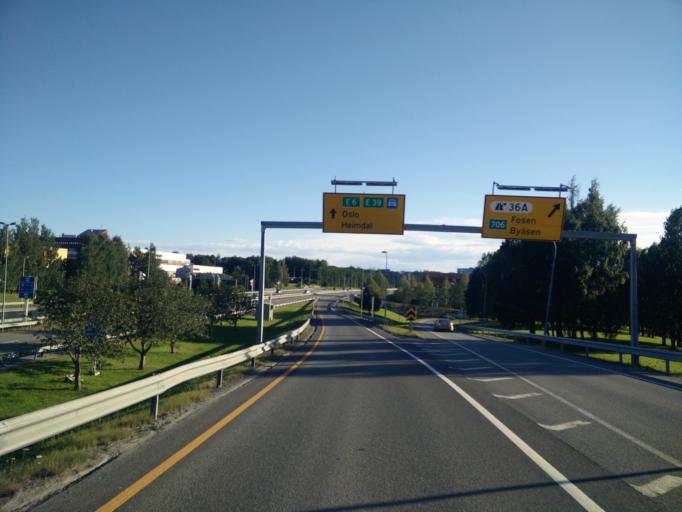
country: NO
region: Sor-Trondelag
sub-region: Trondheim
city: Trondheim
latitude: 63.3992
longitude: 10.3936
